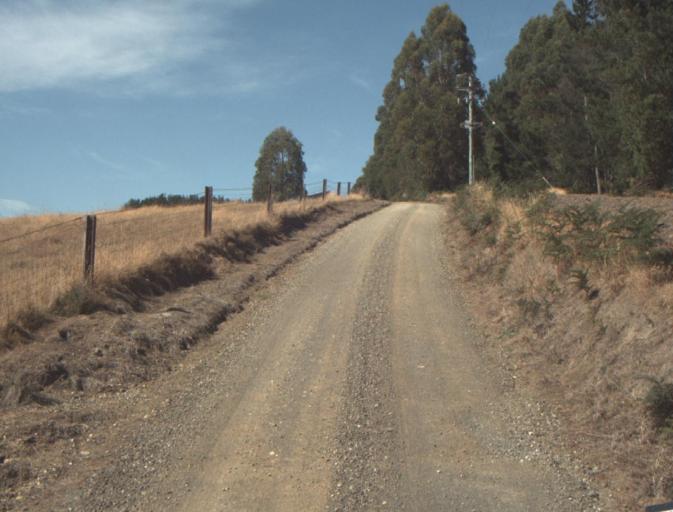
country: AU
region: Tasmania
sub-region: Launceston
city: Mayfield
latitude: -41.1612
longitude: 147.2118
